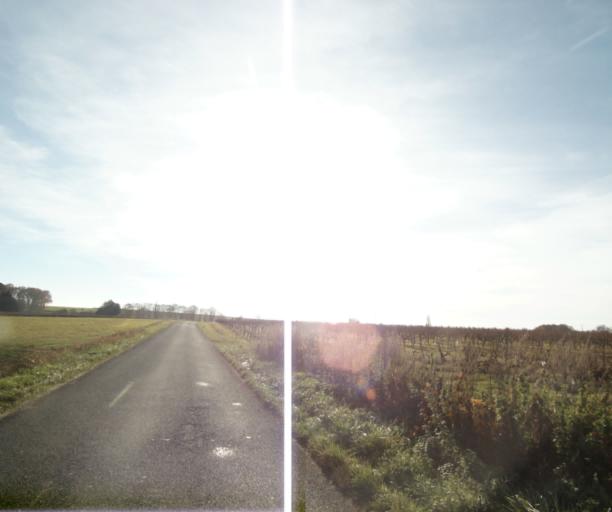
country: FR
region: Poitou-Charentes
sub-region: Departement de la Charente-Maritime
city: Chaniers
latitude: 45.7343
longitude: -0.5487
